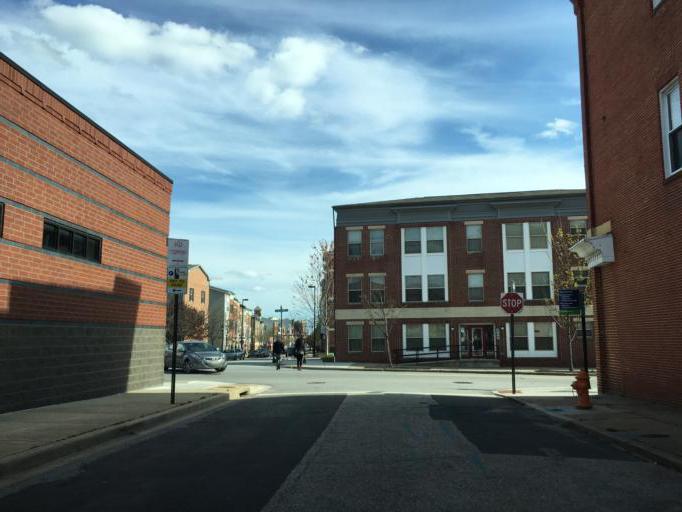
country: US
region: Maryland
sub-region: City of Baltimore
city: Baltimore
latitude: 39.2907
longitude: -76.6034
